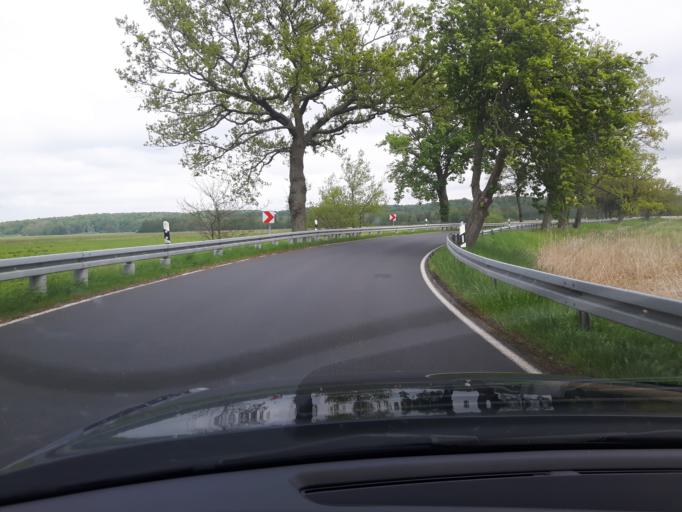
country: DE
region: Mecklenburg-Vorpommern
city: Bad Sulze
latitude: 54.1192
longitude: 12.6808
